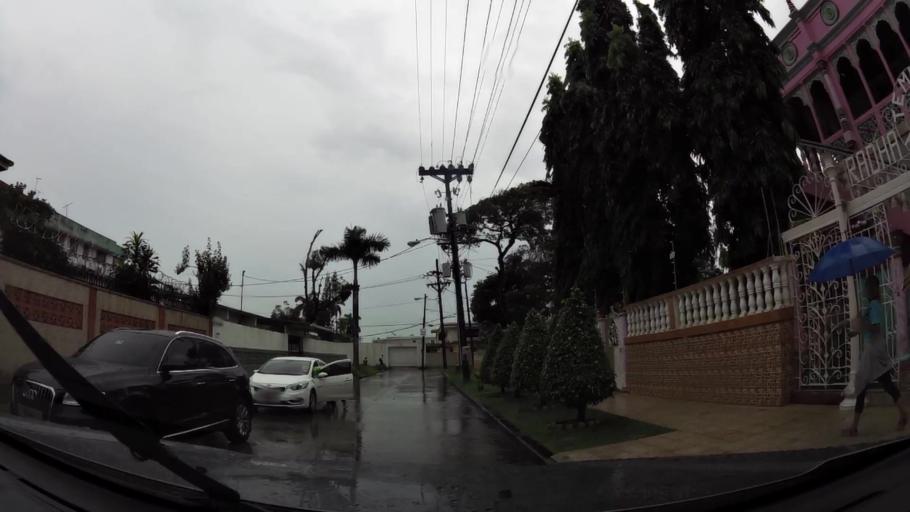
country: PA
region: Colon
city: Colon
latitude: 9.3625
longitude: -79.8973
